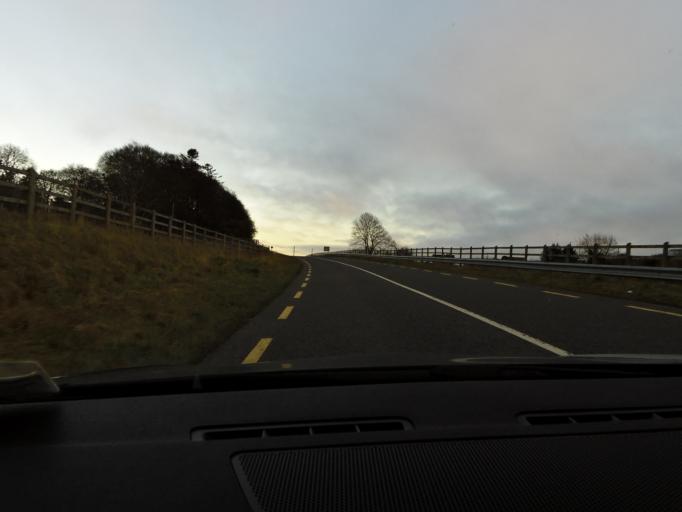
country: IE
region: Connaught
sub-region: Sligo
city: Ballymote
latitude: 53.9826
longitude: -8.4677
